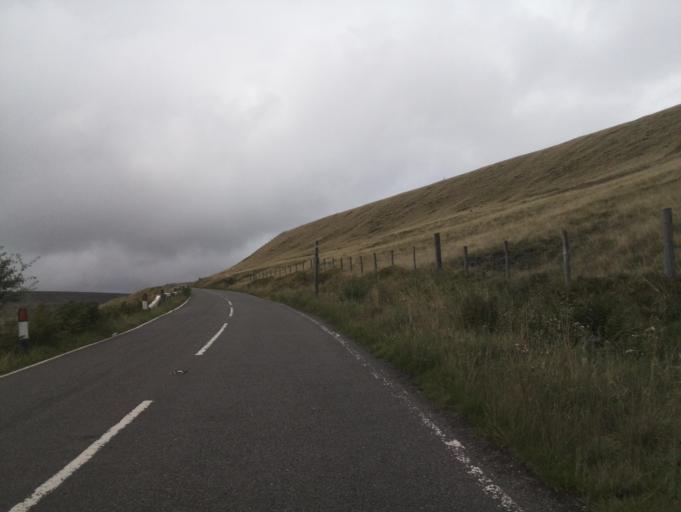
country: GB
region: England
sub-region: Kirklees
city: Meltham
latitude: 53.5242
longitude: -1.8524
